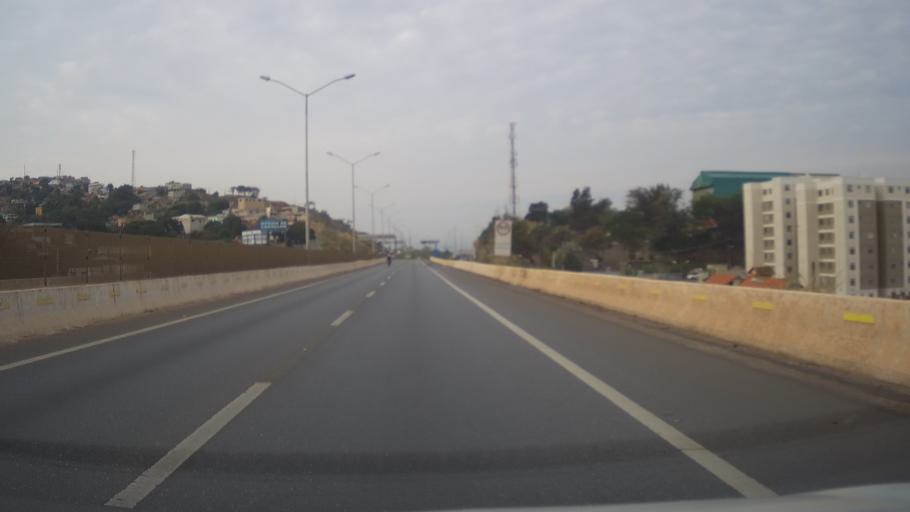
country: BR
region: Minas Gerais
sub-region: Vespasiano
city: Vespasiano
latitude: -19.7556
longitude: -43.9478
